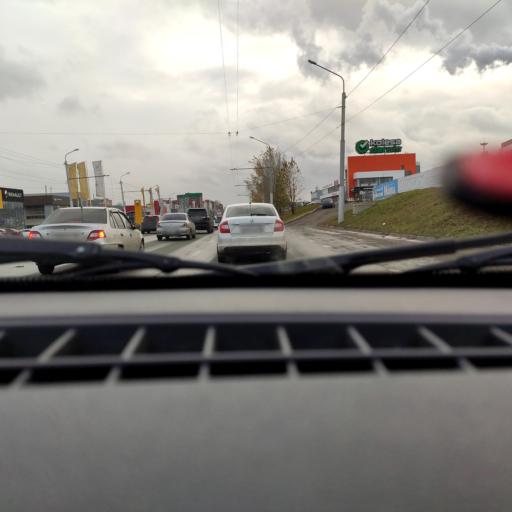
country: RU
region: Bashkortostan
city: Ufa
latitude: 54.7853
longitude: 56.0758
